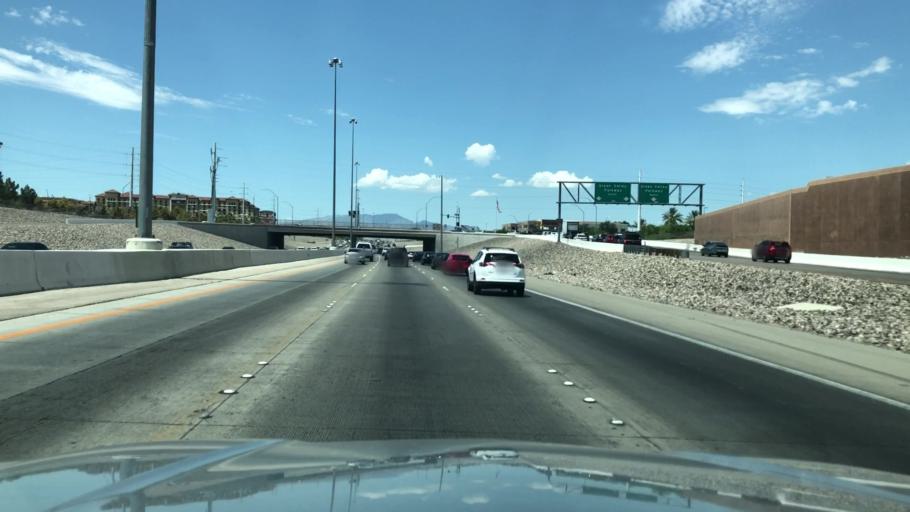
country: US
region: Nevada
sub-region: Clark County
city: Whitney
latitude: 36.0251
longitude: -115.0816
